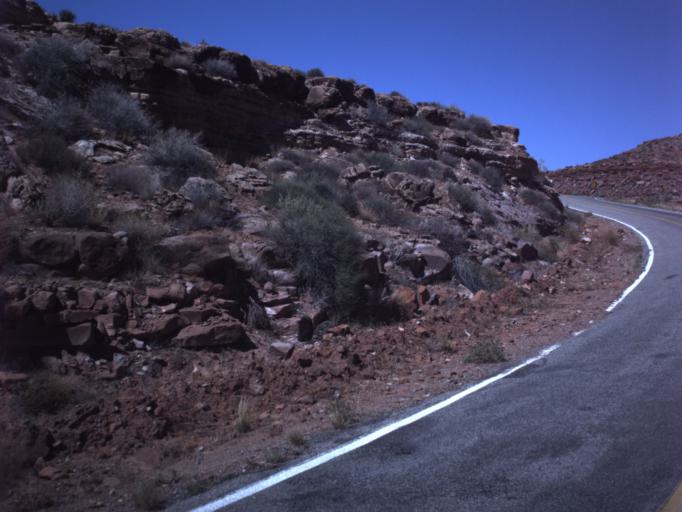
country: US
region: Arizona
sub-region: Navajo County
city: Kayenta
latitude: 37.1926
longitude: -109.9107
